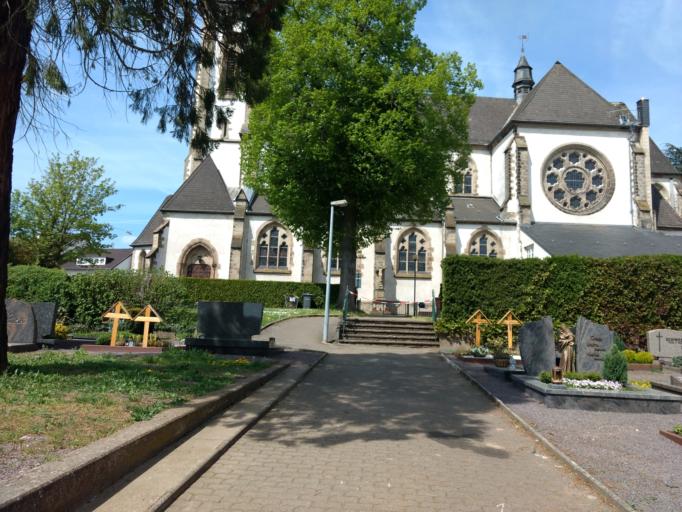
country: DE
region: Saarland
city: Schwalbach
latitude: 49.3034
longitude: 6.8165
